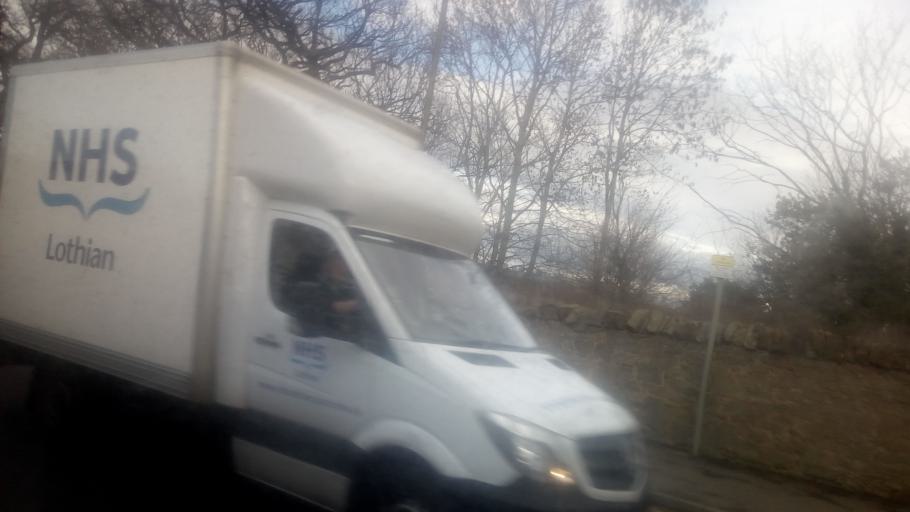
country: GB
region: Scotland
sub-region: Midlothian
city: Loanhead
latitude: 55.9163
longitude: -3.1309
